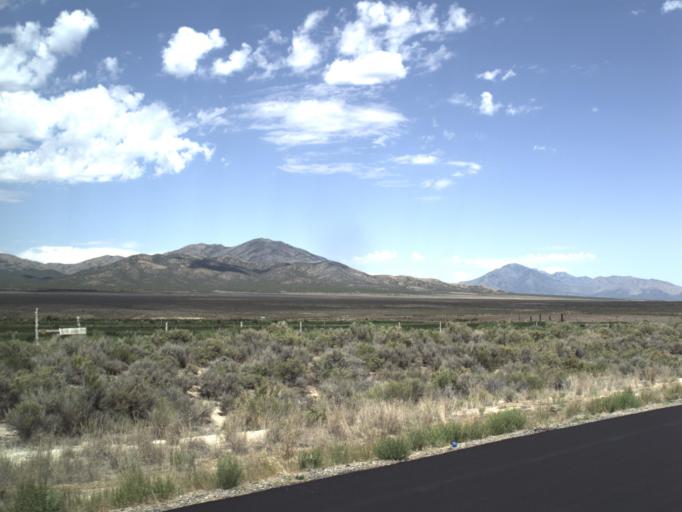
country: US
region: Utah
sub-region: Tooele County
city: Tooele
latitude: 40.1540
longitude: -112.4307
